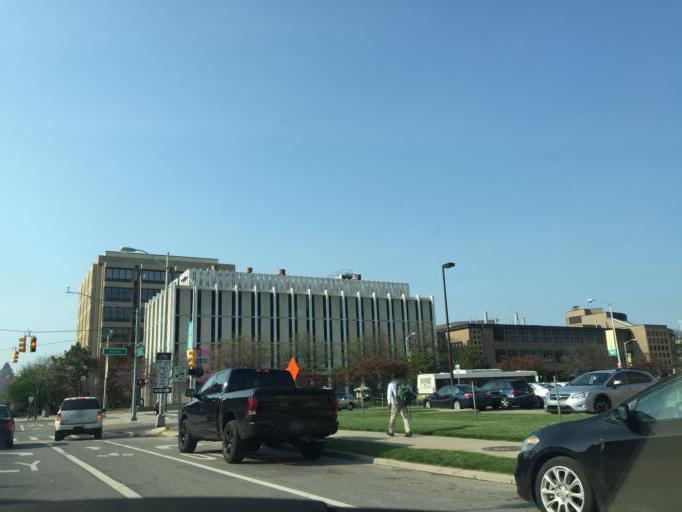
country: US
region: Michigan
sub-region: Wayne County
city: Detroit
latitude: 42.3548
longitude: -83.0686
